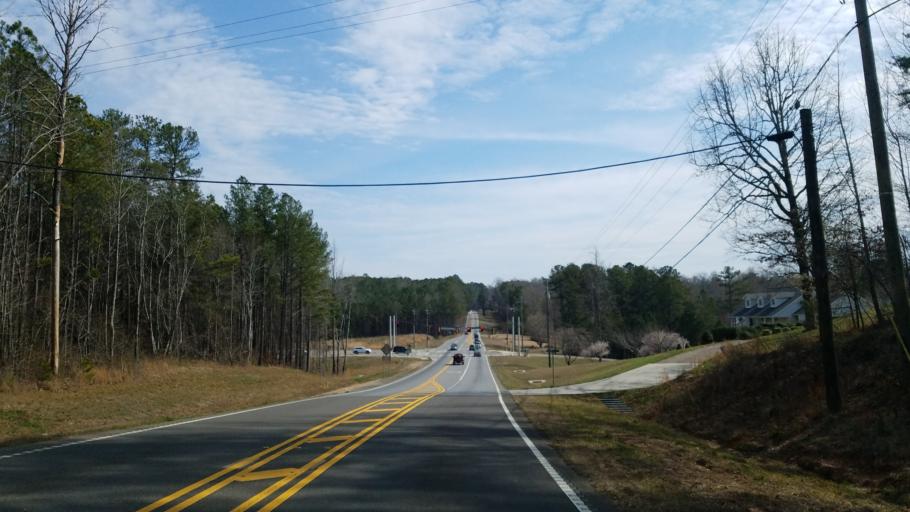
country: US
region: Georgia
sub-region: Cherokee County
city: Canton
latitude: 34.2199
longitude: -84.4622
